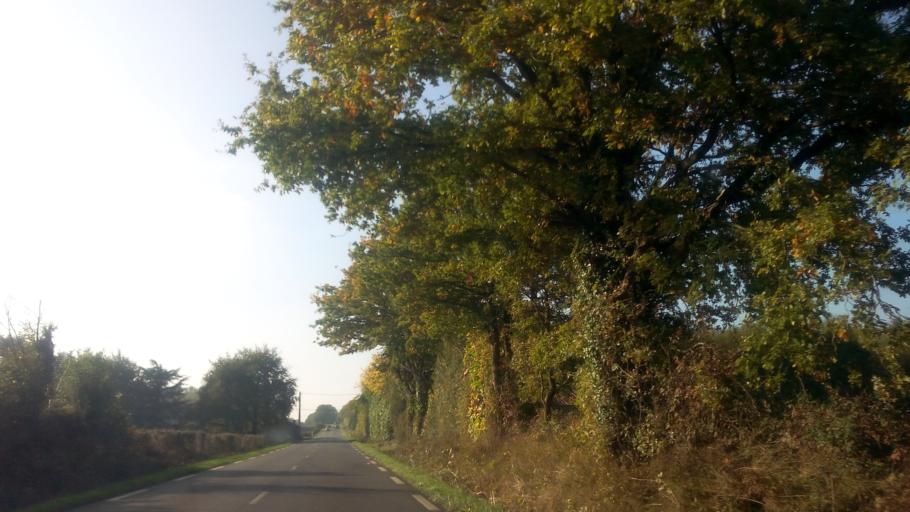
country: FR
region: Pays de la Loire
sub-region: Departement de la Loire-Atlantique
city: Avessac
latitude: 47.6393
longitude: -1.9984
